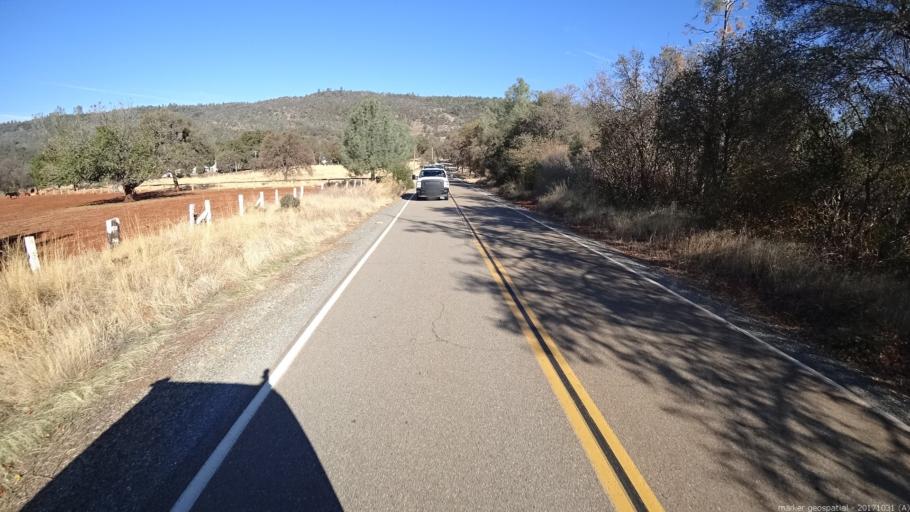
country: US
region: California
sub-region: Shasta County
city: Shingletown
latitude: 40.4516
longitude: -121.8995
